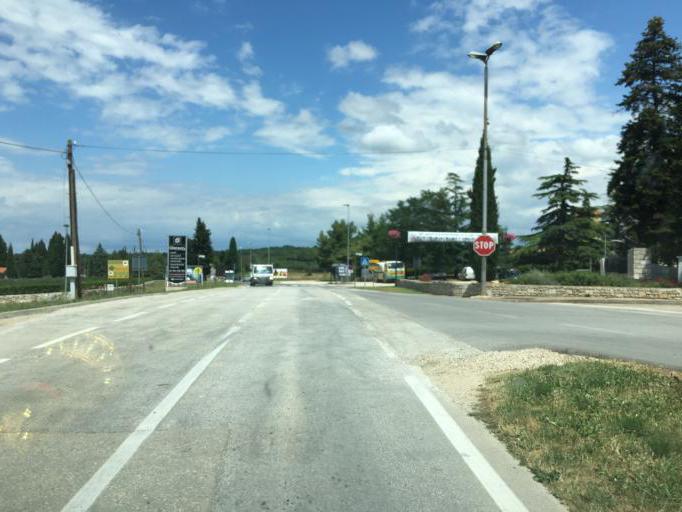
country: HR
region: Istarska
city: Vrsar
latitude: 45.1768
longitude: 13.7424
